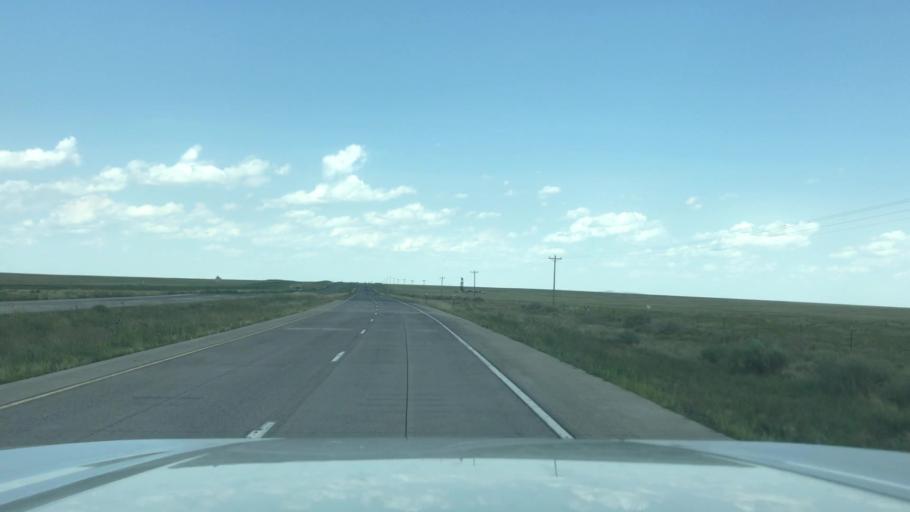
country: US
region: New Mexico
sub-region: Union County
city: Clayton
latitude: 36.6133
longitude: -103.6794
